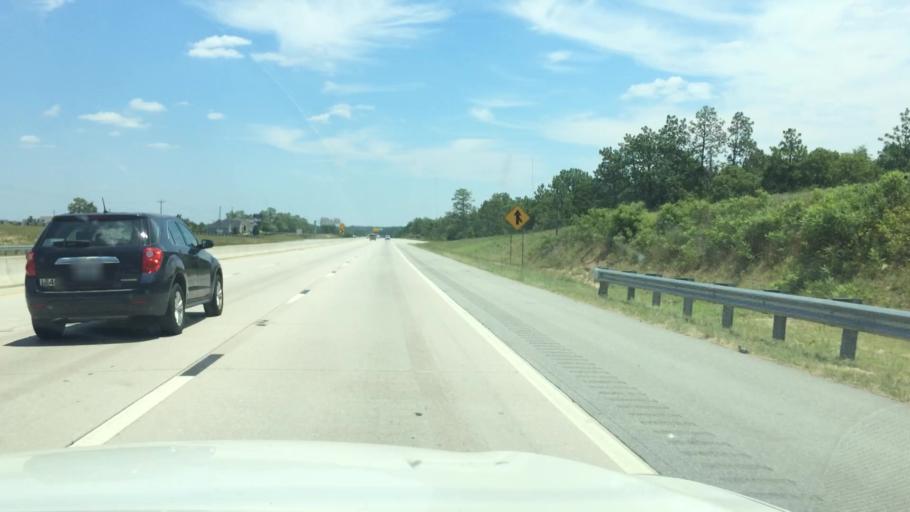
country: US
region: South Carolina
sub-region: Kershaw County
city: Elgin
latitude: 34.1048
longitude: -80.8291
